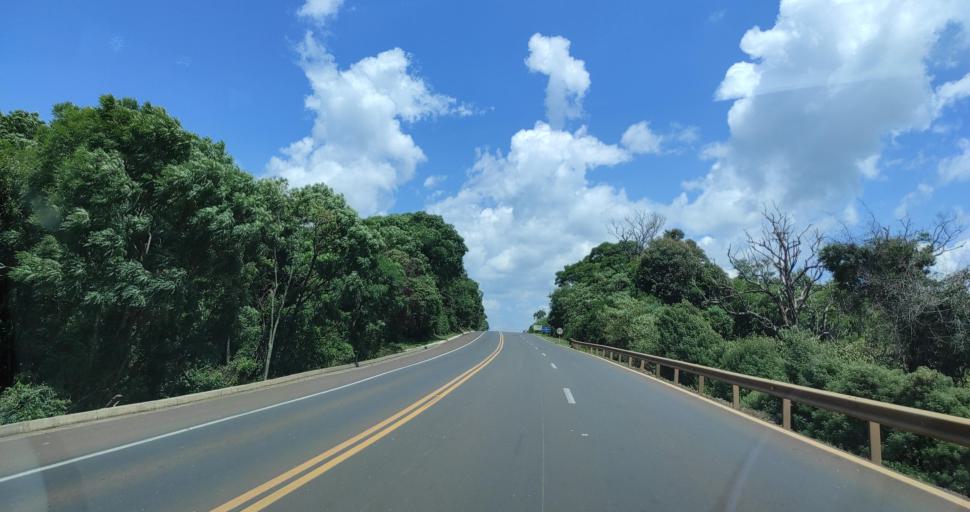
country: BR
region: Santa Catarina
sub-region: Xanxere
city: Xanxere
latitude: -26.8791
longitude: -52.3512
